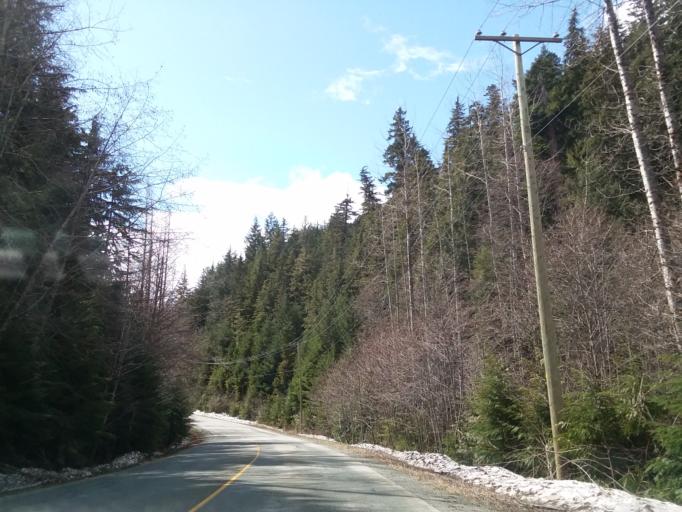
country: CA
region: British Columbia
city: Whistler
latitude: 50.1268
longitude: -122.9865
